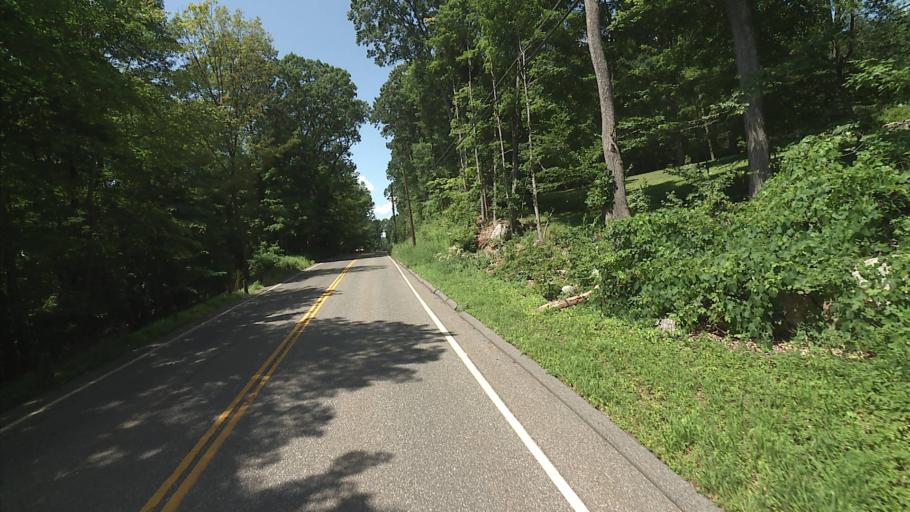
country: US
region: Connecticut
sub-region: Litchfield County
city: Litchfield
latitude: 41.8545
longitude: -73.3185
